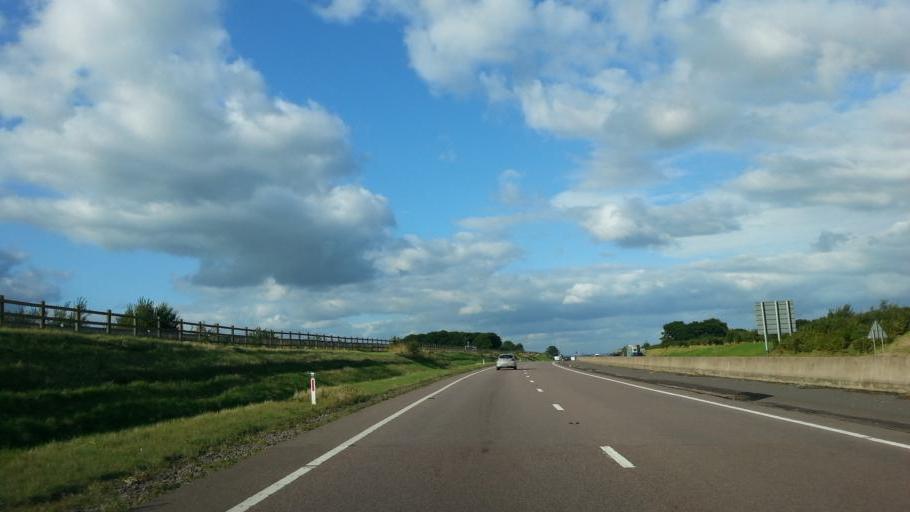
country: GB
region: England
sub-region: Nottinghamshire
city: Farndon
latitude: 53.0164
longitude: -0.9029
